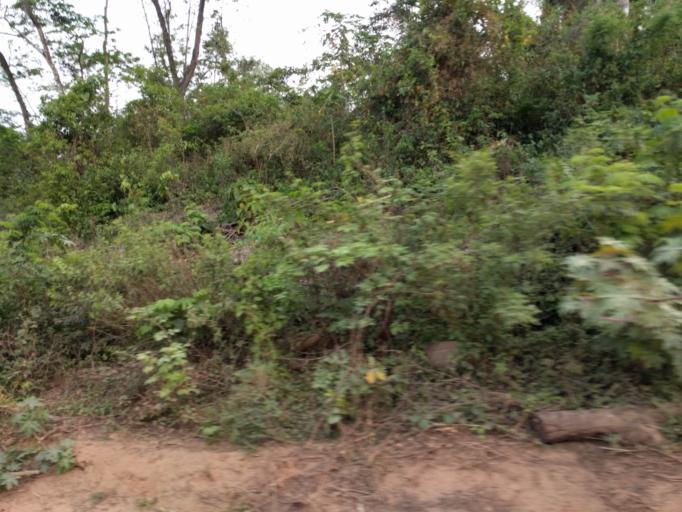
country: BO
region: Santa Cruz
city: Santa Rita
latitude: -17.9325
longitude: -63.3682
